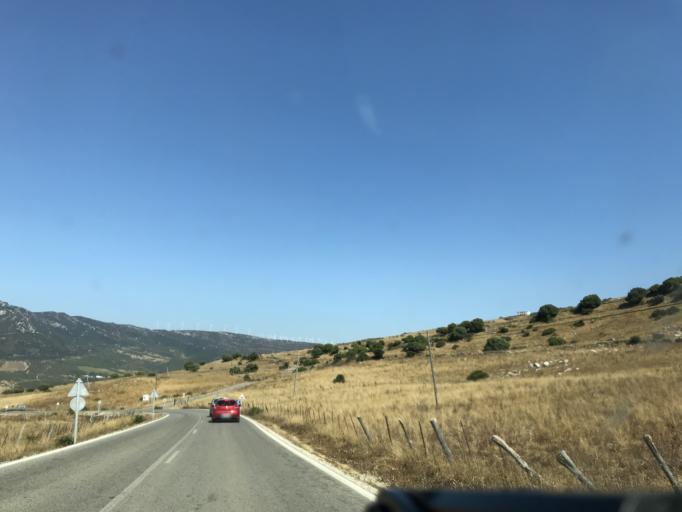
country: ES
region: Andalusia
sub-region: Provincia de Cadiz
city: Zahara de los Atunes
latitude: 36.1004
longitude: -5.7321
